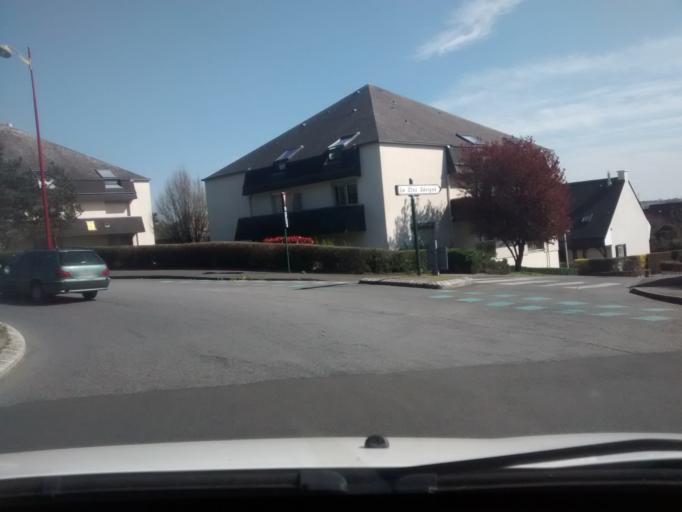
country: FR
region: Brittany
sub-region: Departement d'Ille-et-Vilaine
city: Chantepie
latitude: 48.1140
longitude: -1.6340
